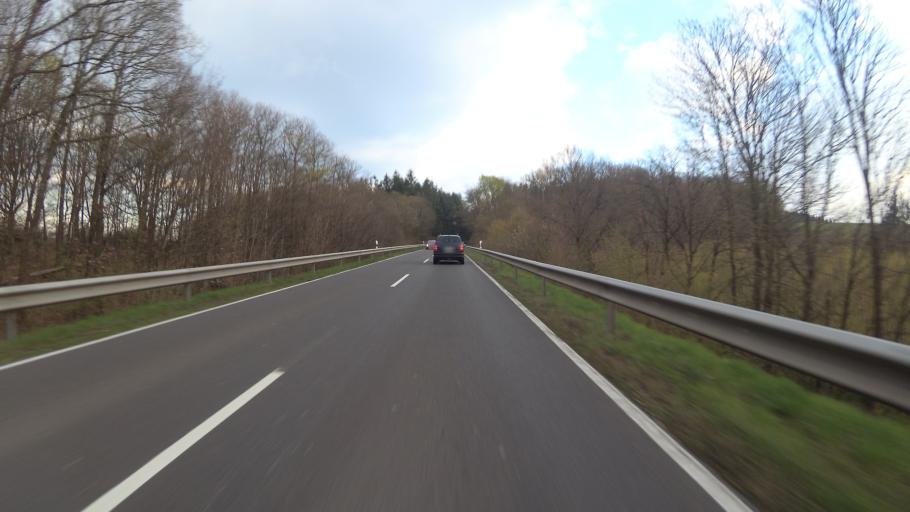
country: DE
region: Rheinland-Pfalz
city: Veldenz
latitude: 49.8949
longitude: 7.0387
